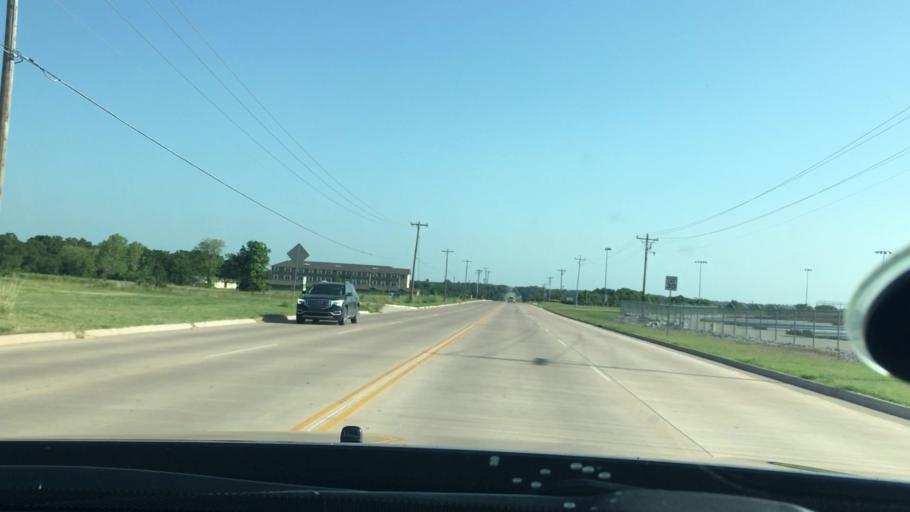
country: US
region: Oklahoma
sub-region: Pontotoc County
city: Ada
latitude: 34.7924
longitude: -96.6524
